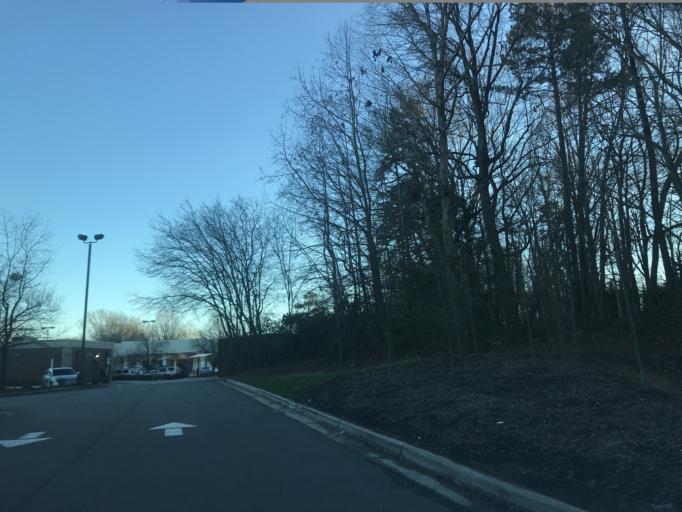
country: US
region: North Carolina
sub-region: Wake County
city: Raleigh
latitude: 35.8605
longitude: -78.5830
